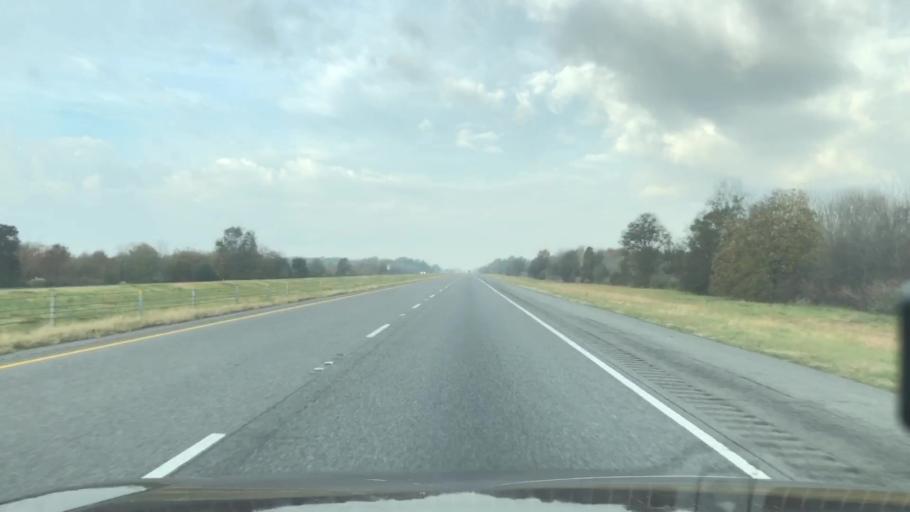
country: US
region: Louisiana
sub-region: Madison Parish
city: Tallulah
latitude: 32.4200
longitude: -91.3078
